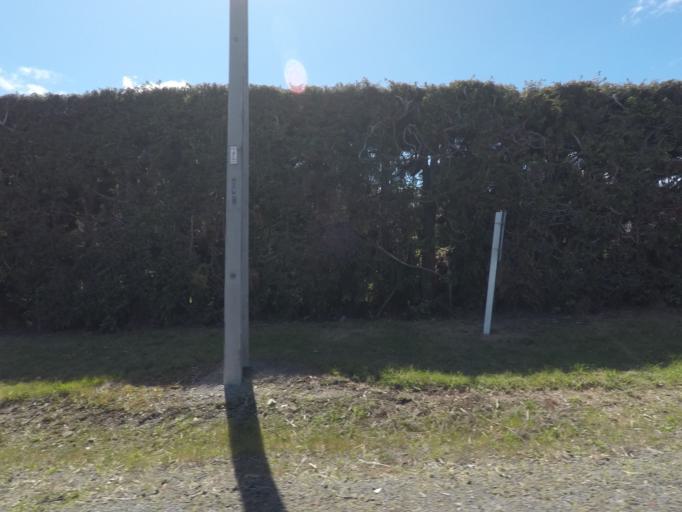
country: NZ
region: Auckland
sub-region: Auckland
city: Rosebank
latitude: -36.7785
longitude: 174.5781
